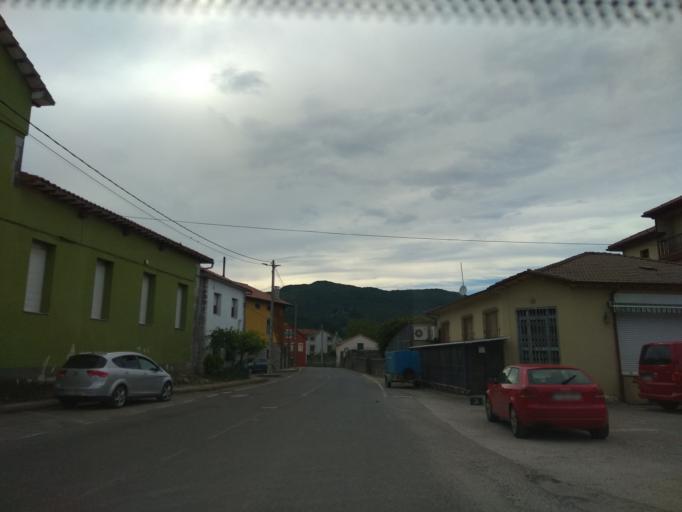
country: ES
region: Cantabria
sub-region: Provincia de Cantabria
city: Hazas de Cesto
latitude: 43.3973
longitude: -3.5883
